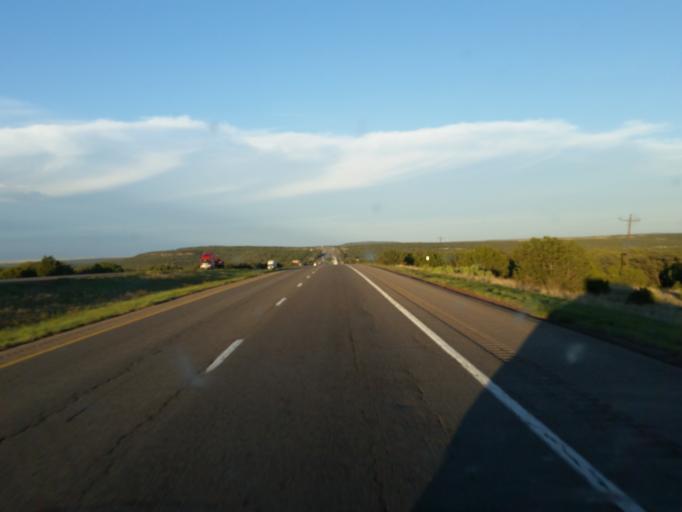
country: US
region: New Mexico
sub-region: Torrance County
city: Moriarty
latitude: 35.0039
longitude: -105.5904
